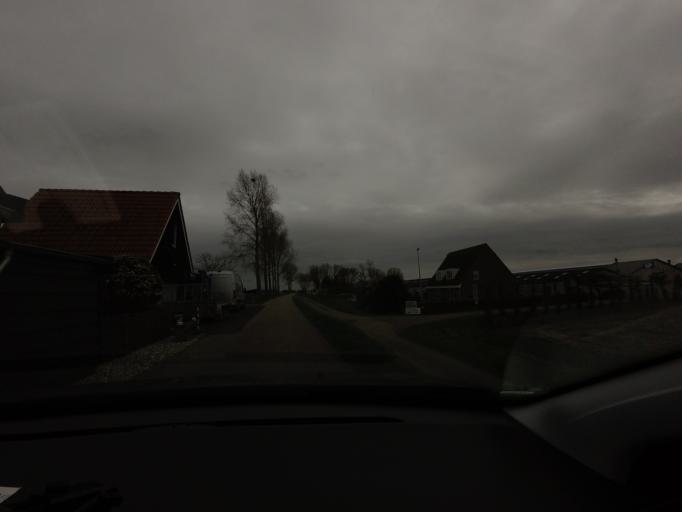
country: NL
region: South Holland
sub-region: Gemeente Goeree-Overflakkee
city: Middelharnis
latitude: 51.7295
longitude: 4.2235
